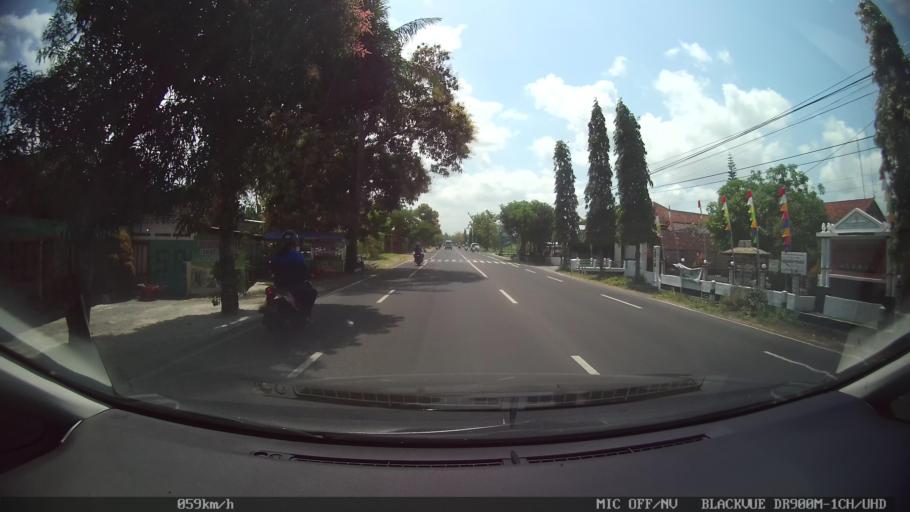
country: ID
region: Daerah Istimewa Yogyakarta
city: Pandak
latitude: -7.9190
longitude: 110.2830
